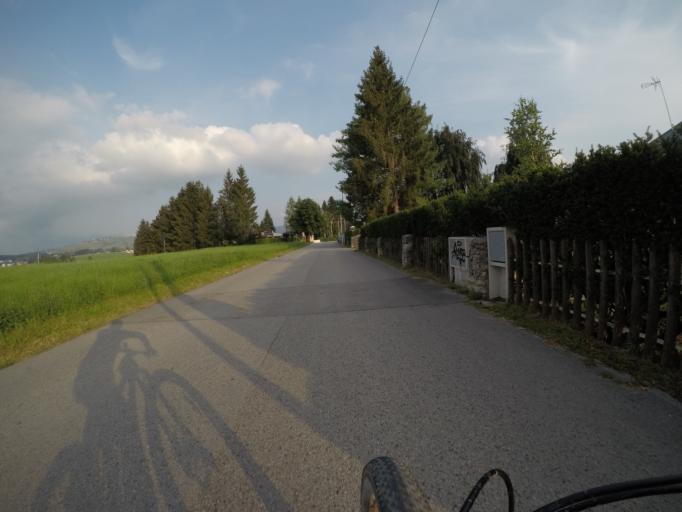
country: IT
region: Veneto
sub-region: Provincia di Vicenza
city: Asiago
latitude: 45.8826
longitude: 11.5038
